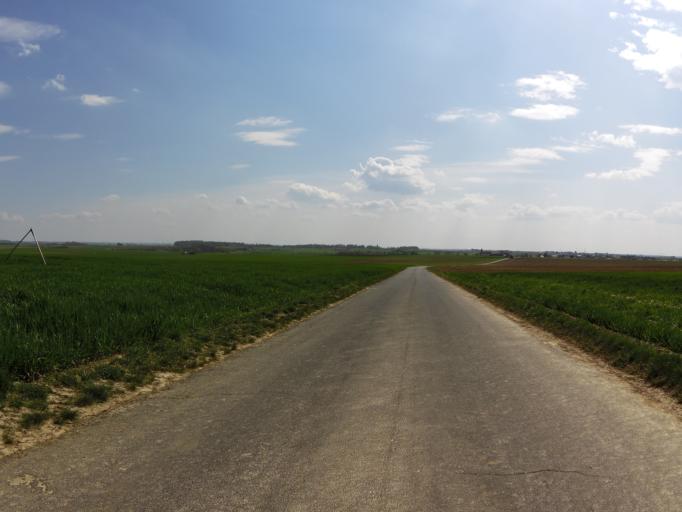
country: DE
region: Bavaria
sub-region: Regierungsbezirk Unterfranken
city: Giebelstadt
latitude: 49.6827
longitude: 9.9633
